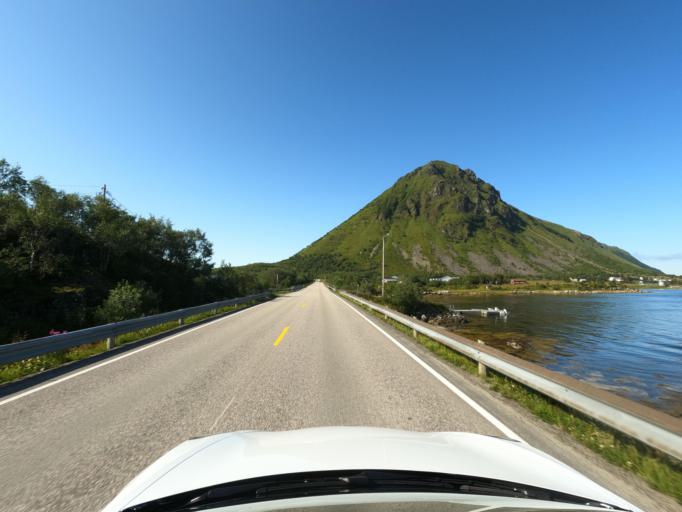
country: NO
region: Nordland
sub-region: Vestvagoy
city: Evjen
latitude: 68.2695
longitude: 13.9742
